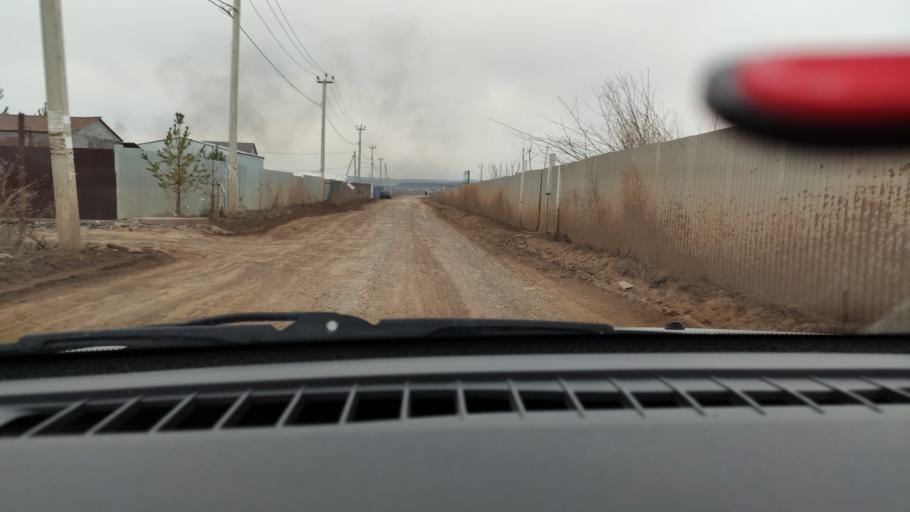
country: RU
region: Perm
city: Kultayevo
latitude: 57.8989
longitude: 55.9977
